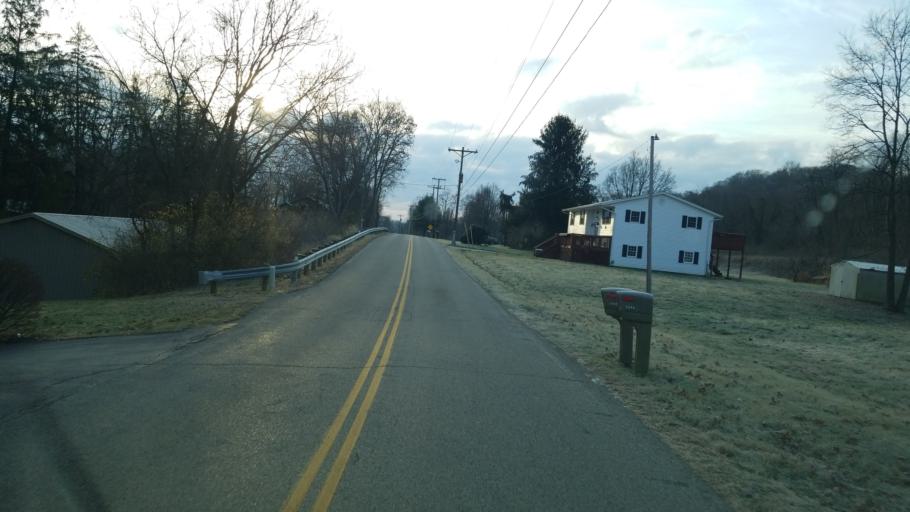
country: US
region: Ohio
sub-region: Ross County
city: Chillicothe
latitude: 39.2713
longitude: -82.9263
